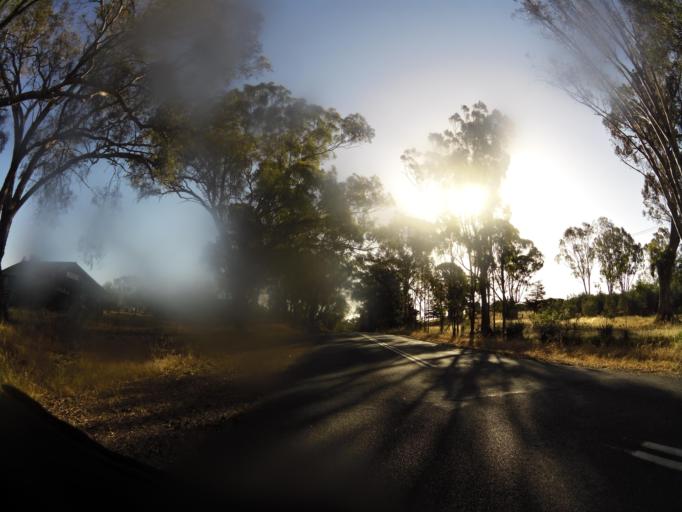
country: AU
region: Victoria
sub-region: Murrindindi
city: Kinglake West
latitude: -37.0209
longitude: 145.1061
